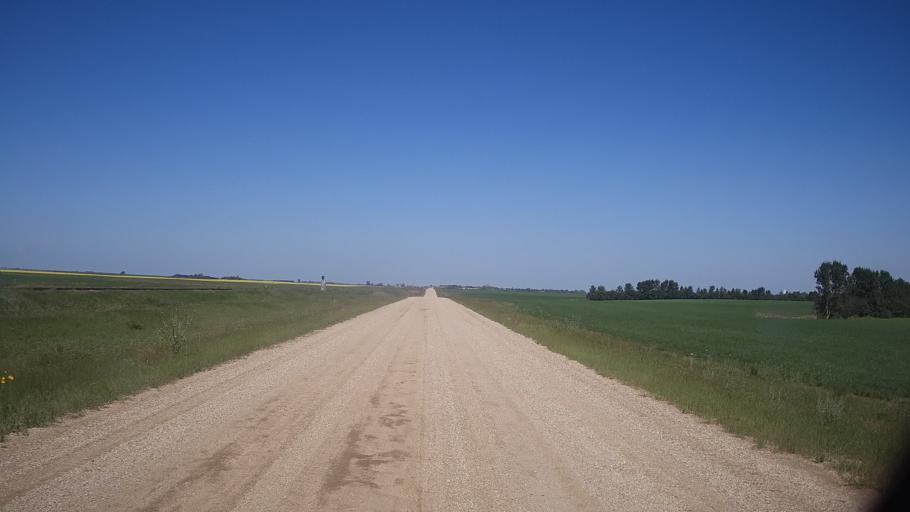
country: CA
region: Saskatchewan
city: Watrous
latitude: 51.8755
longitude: -106.0072
